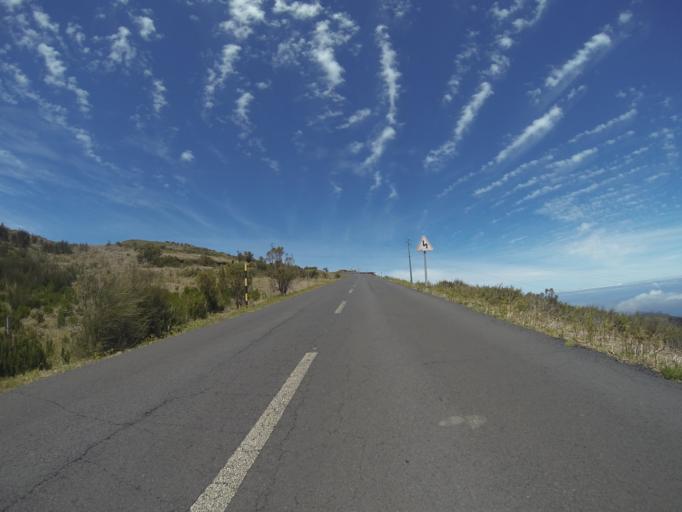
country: PT
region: Madeira
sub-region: Funchal
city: Nossa Senhora do Monte
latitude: 32.7169
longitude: -16.9046
